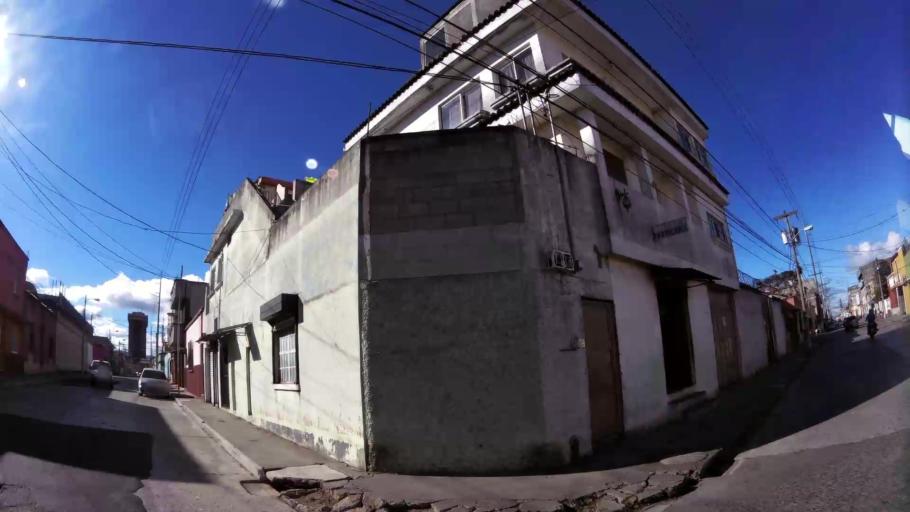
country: GT
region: Guatemala
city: Guatemala City
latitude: 14.6275
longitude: -90.5075
